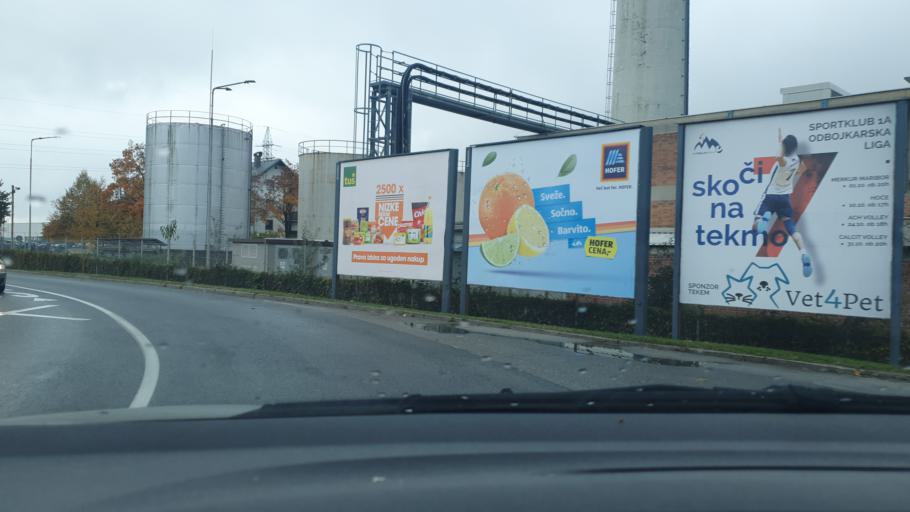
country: SI
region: Kranj
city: Kranj
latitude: 46.2352
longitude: 14.3663
